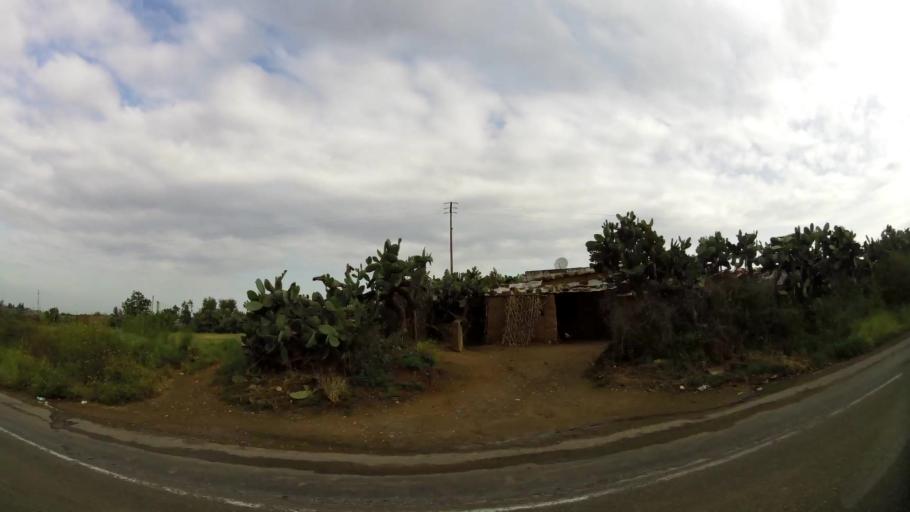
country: MA
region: Rabat-Sale-Zemmour-Zaer
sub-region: Khemisset
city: Khemisset
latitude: 33.7755
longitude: -6.1406
